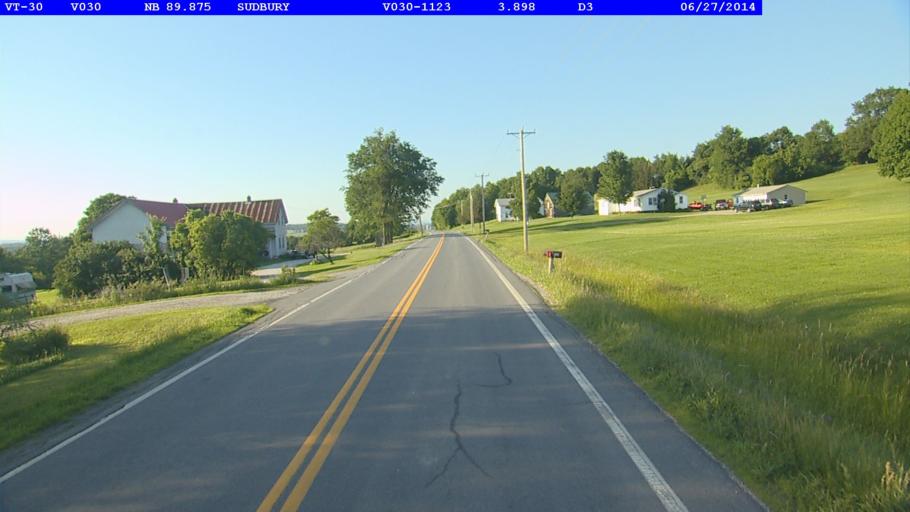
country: US
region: Vermont
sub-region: Rutland County
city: Brandon
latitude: 43.8037
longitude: -73.2024
